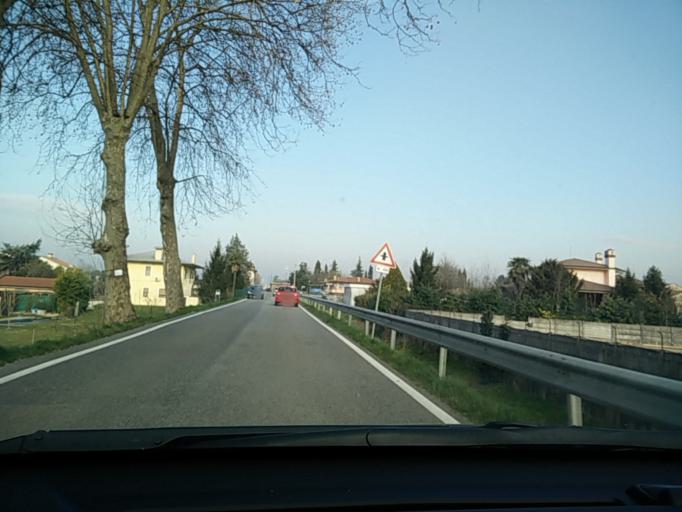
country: IT
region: Veneto
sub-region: Provincia di Treviso
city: Zenson di Piave
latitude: 45.6762
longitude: 12.4898
